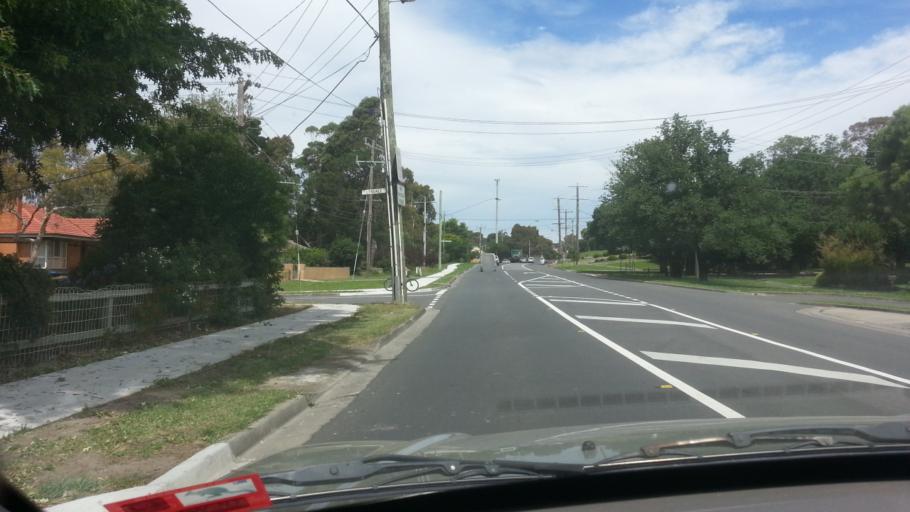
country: AU
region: Victoria
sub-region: Knox
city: Ferntree Gully
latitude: -37.8914
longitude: 145.2901
